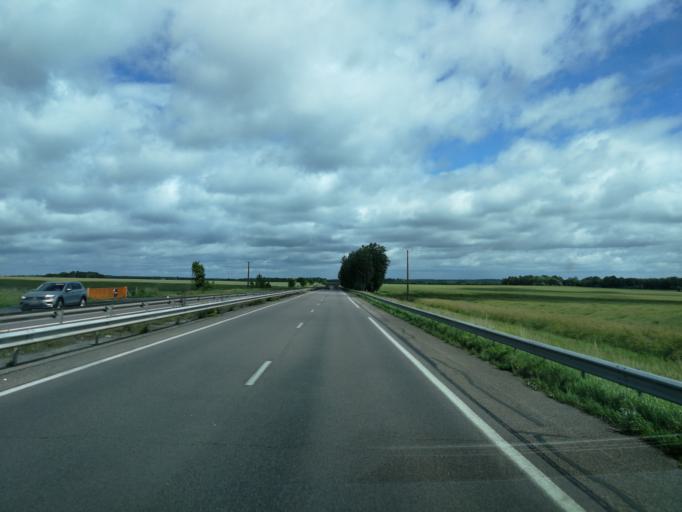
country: FR
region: Haute-Normandie
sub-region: Departement de l'Eure
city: Normanville
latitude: 49.0868
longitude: 1.1885
